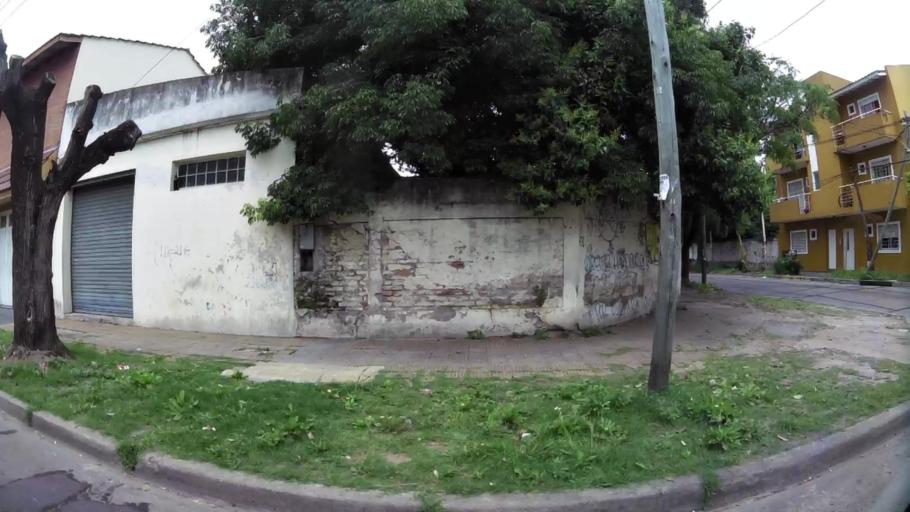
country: AR
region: Buenos Aires
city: San Justo
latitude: -34.6639
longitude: -58.5343
